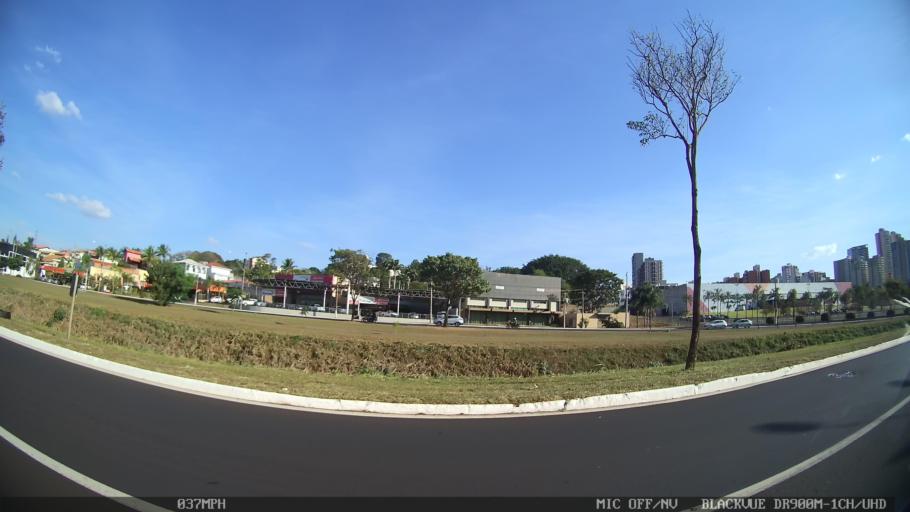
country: BR
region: Sao Paulo
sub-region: Ribeirao Preto
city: Ribeirao Preto
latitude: -21.2088
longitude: -47.7884
